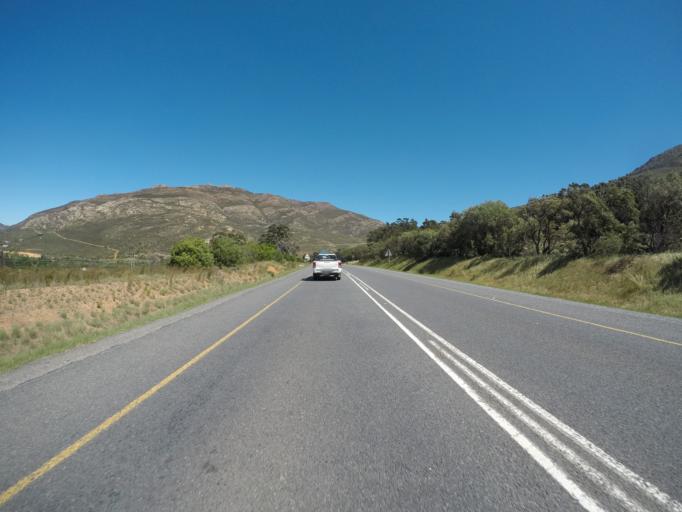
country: ZA
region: Western Cape
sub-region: Cape Winelands District Municipality
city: Ceres
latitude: -33.3140
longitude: 19.0942
